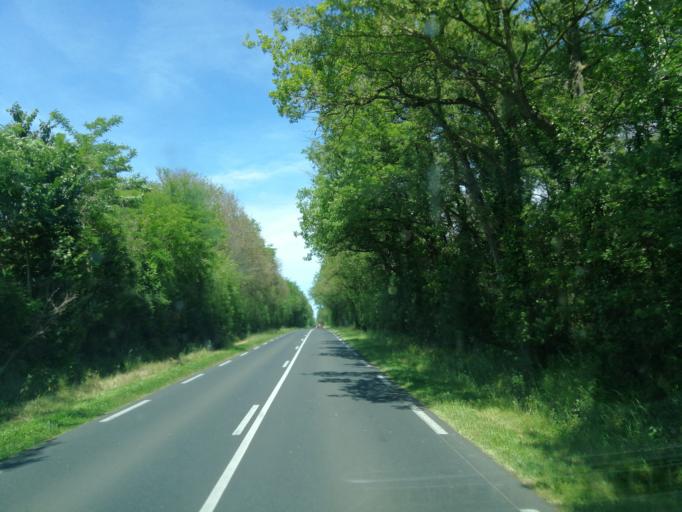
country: FR
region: Poitou-Charentes
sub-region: Departement des Deux-Sevres
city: Saint-Varent
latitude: 46.9323
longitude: -0.2496
